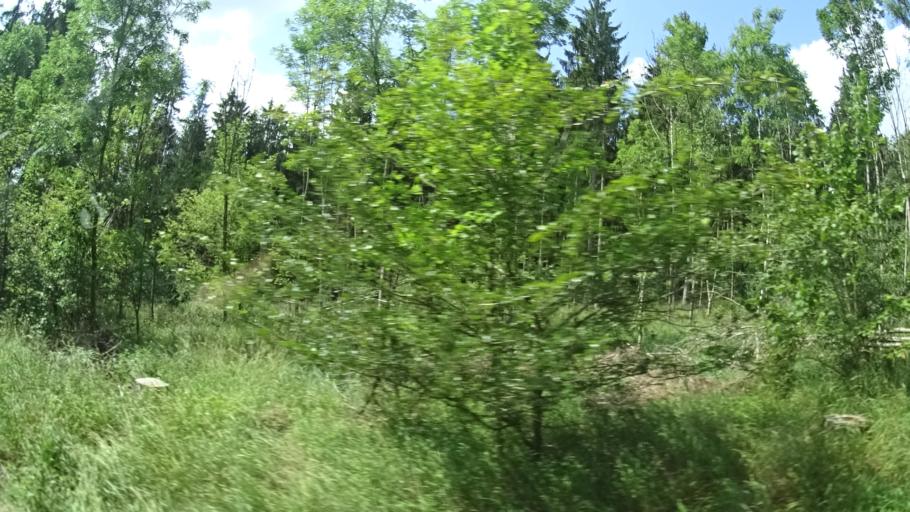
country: DE
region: Thuringia
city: Hildburghausen
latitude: 50.3916
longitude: 10.7665
